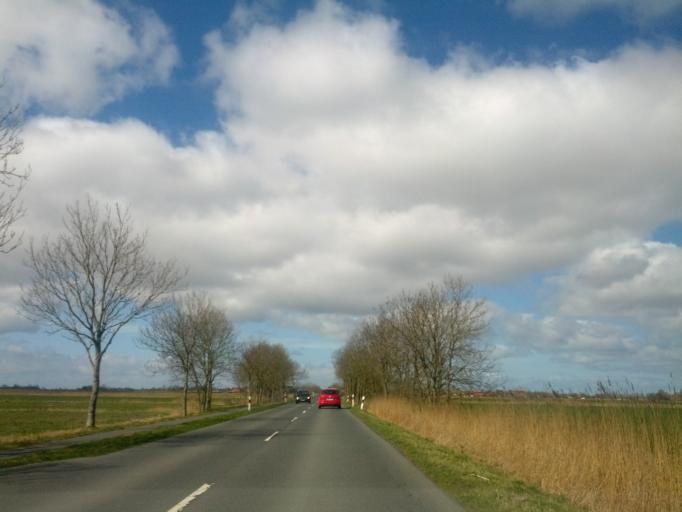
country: DE
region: Lower Saxony
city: Esens
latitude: 53.6665
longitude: 7.5947
